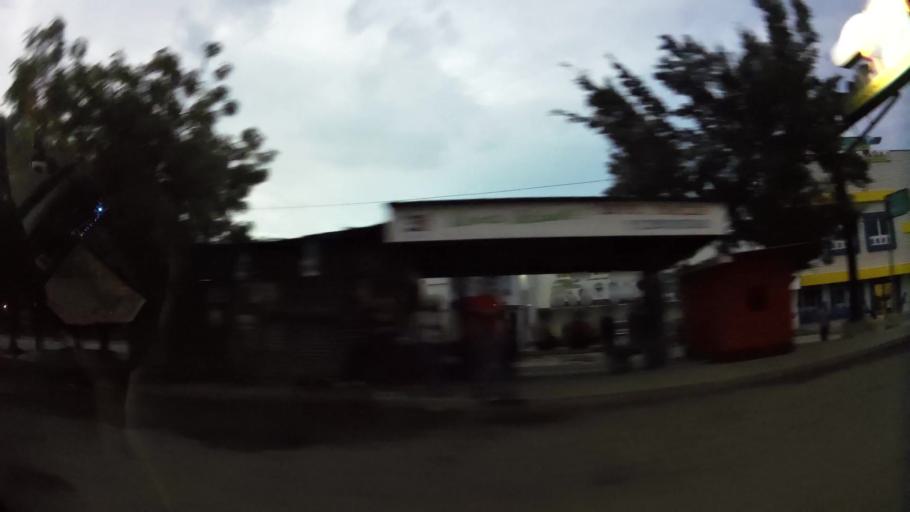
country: NI
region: Esteli
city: Esteli
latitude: 13.1020
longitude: -86.3521
